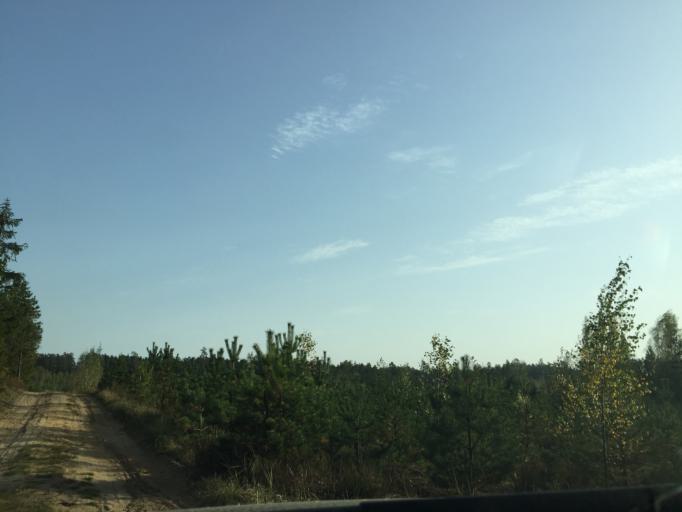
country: LV
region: Garkalne
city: Garkalne
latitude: 56.9699
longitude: 24.4181
